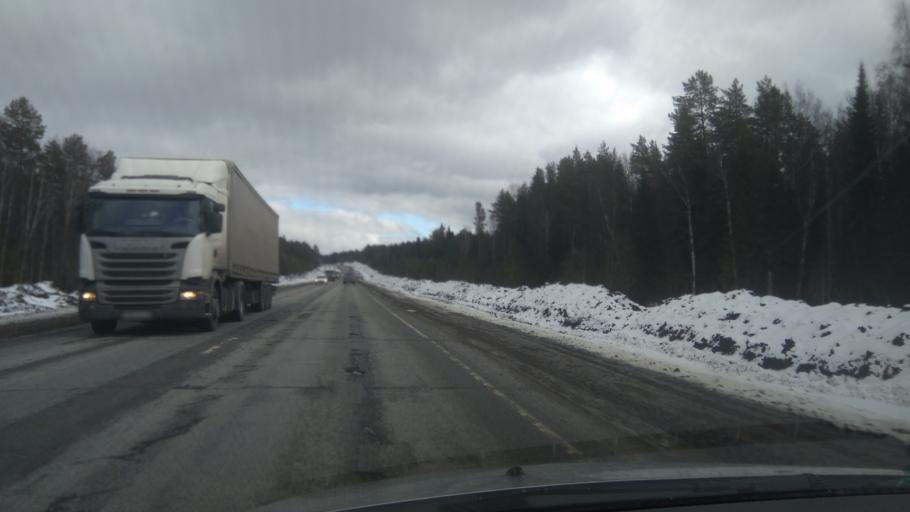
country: RU
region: Sverdlovsk
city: Bisert'
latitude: 56.8296
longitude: 58.9665
